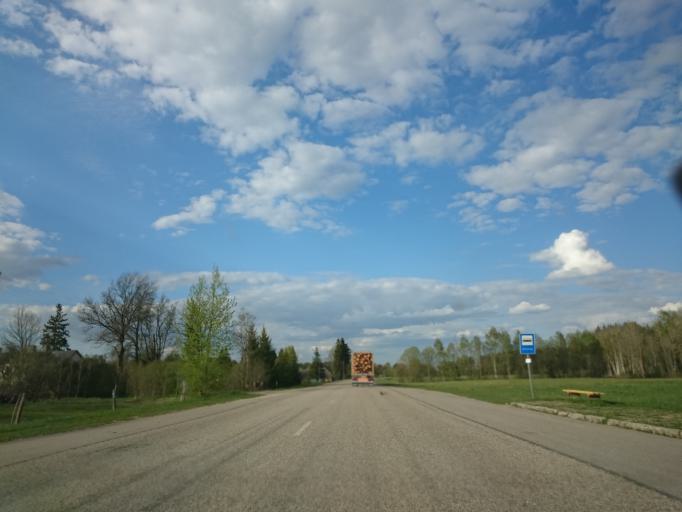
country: LV
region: Aizpute
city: Aizpute
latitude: 56.7771
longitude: 21.6349
